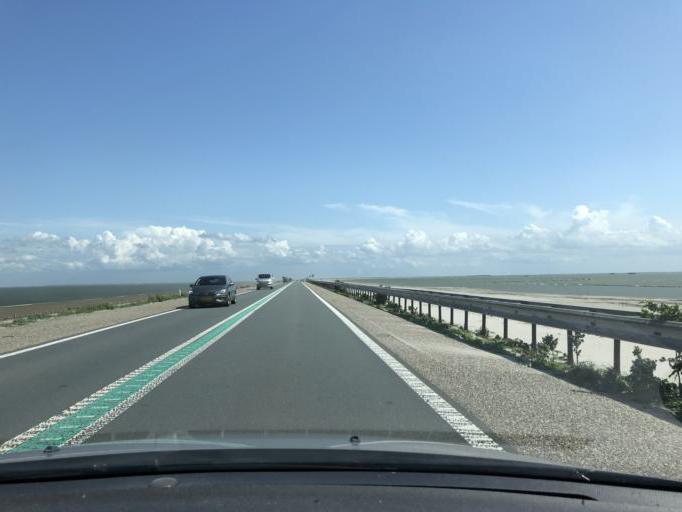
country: NL
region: North Holland
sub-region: Gemeente Enkhuizen
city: Enkhuizen
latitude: 52.6849
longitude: 5.3258
